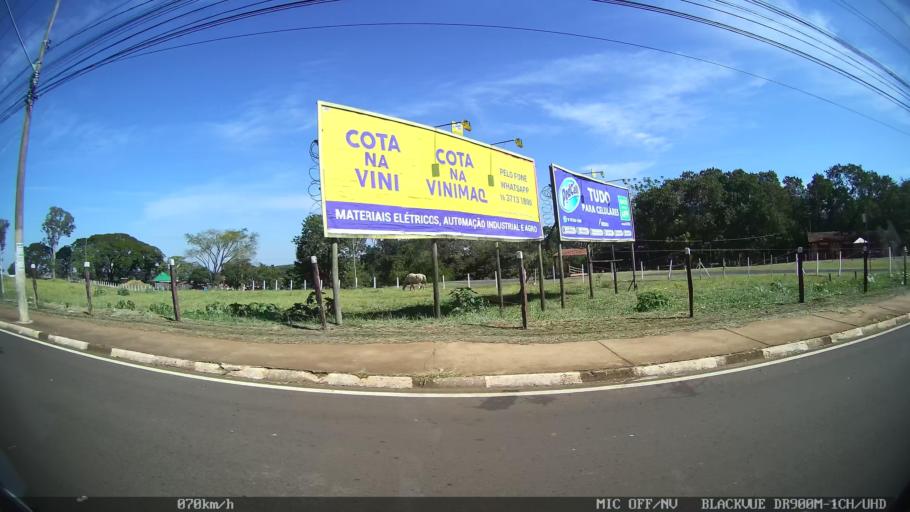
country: BR
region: Sao Paulo
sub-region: Franca
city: Franca
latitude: -20.5452
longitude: -47.4206
